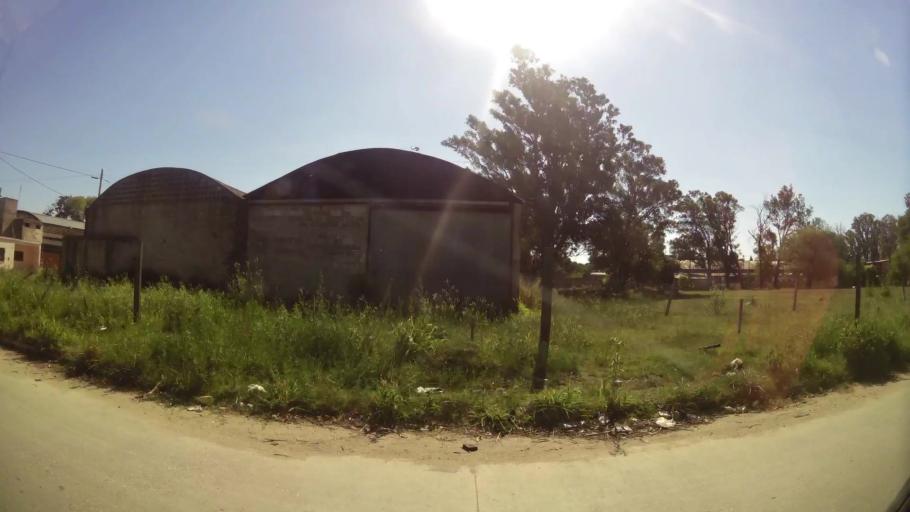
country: AR
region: Cordoba
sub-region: Departamento de Capital
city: Cordoba
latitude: -31.4080
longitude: -64.1456
